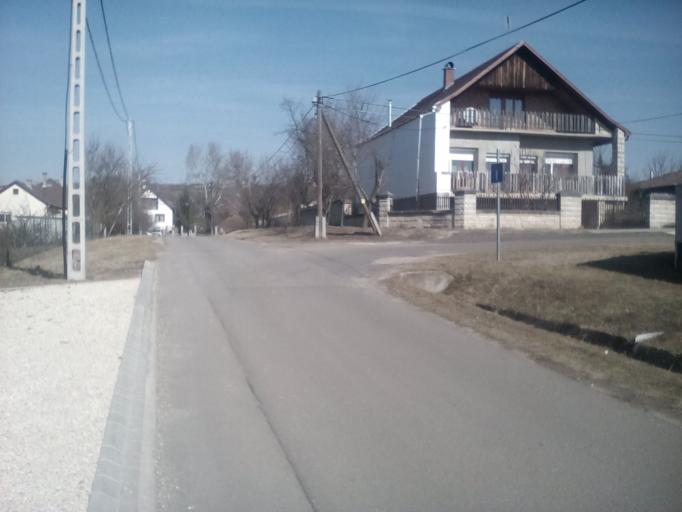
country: HU
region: Pest
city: Soskut
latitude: 47.4021
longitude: 18.8377
